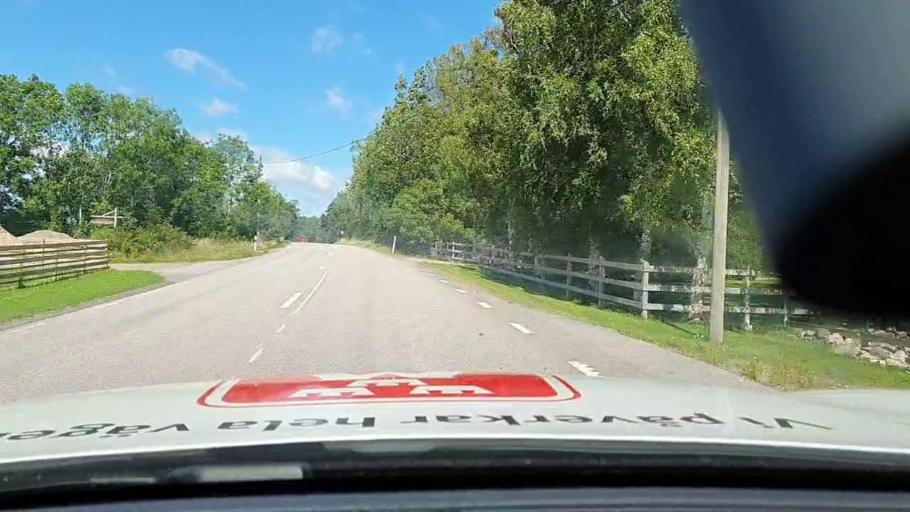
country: SE
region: Vaestra Goetaland
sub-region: Skovde Kommun
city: Stopen
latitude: 58.5173
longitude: 13.9785
